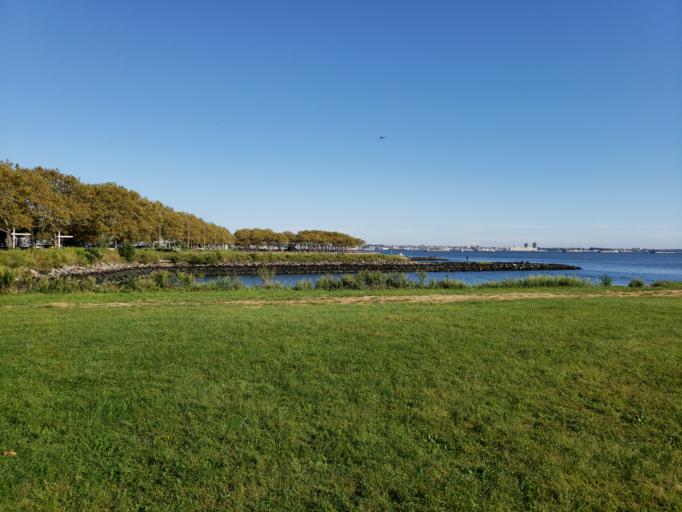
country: US
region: New Jersey
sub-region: Hudson County
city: Jersey City
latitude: 40.6944
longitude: -74.0608
